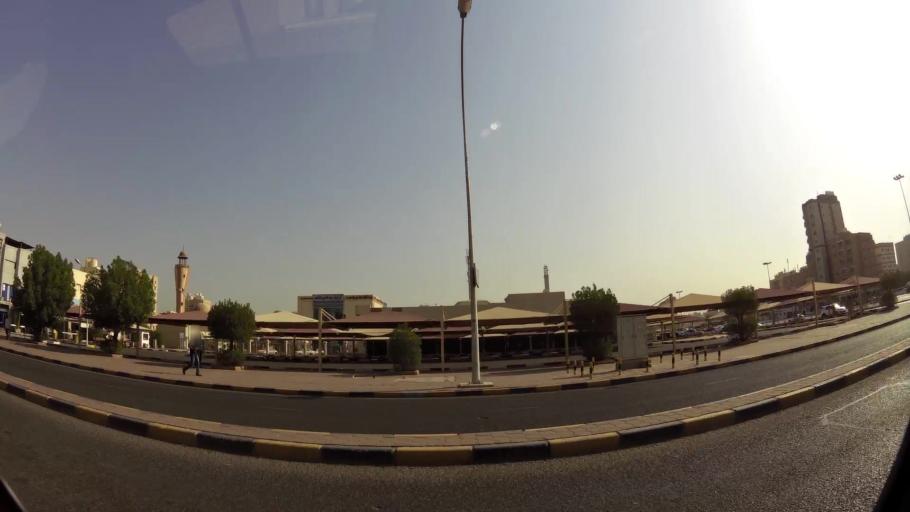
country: KW
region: Muhafazat Hawalli
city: Hawalli
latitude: 29.3328
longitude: 48.0092
